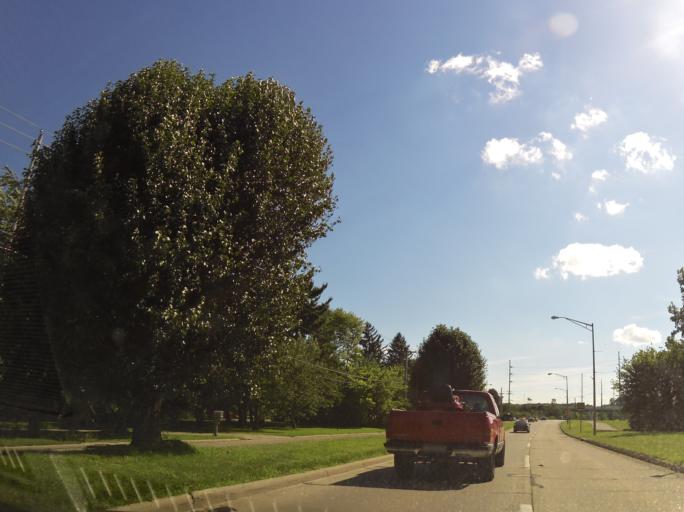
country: US
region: Ohio
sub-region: Greene County
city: Wright-Patterson AFB
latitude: 39.7955
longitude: -84.0429
